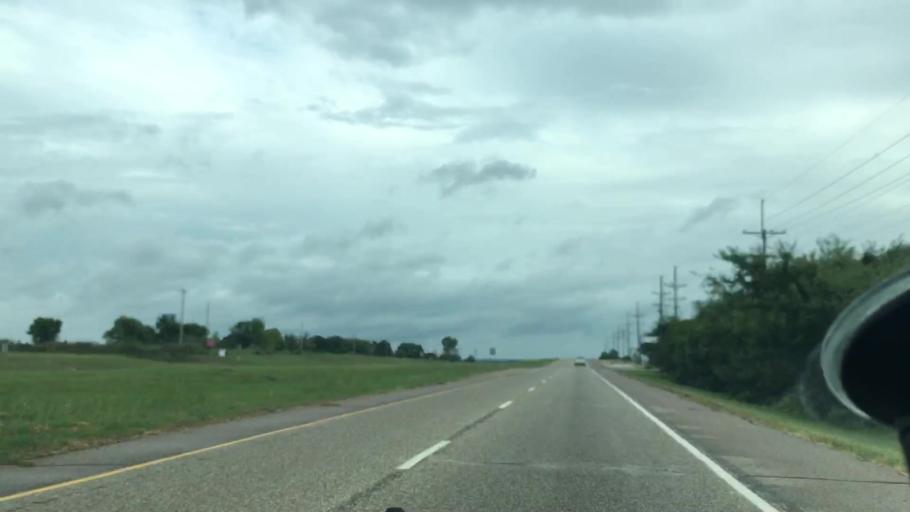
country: US
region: Oklahoma
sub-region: Seminole County
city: Seminole
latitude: 35.2915
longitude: -96.6713
